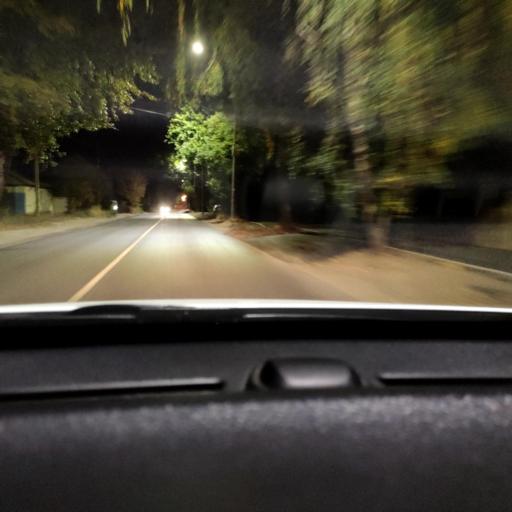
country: RU
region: Voronezj
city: Somovo
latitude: 51.7363
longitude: 39.2669
